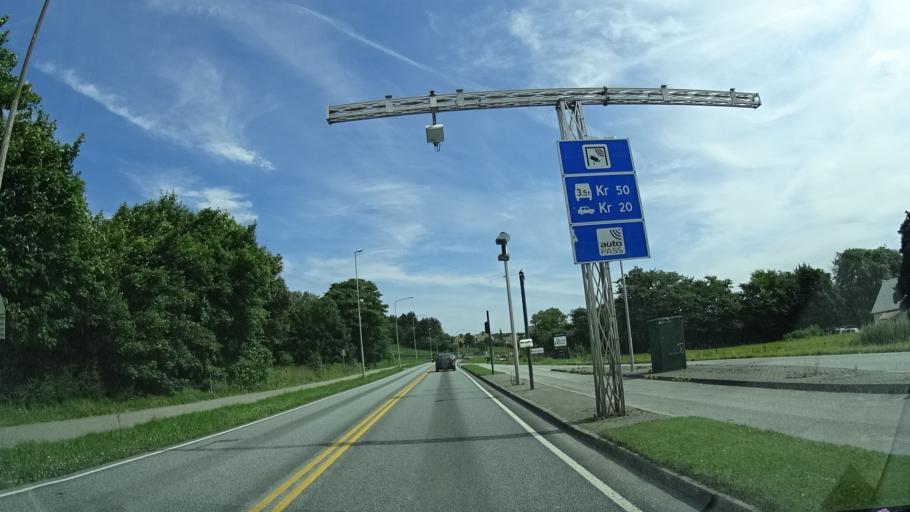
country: NO
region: Rogaland
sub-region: Randaberg
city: Randaberg
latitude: 58.9834
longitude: 5.6719
